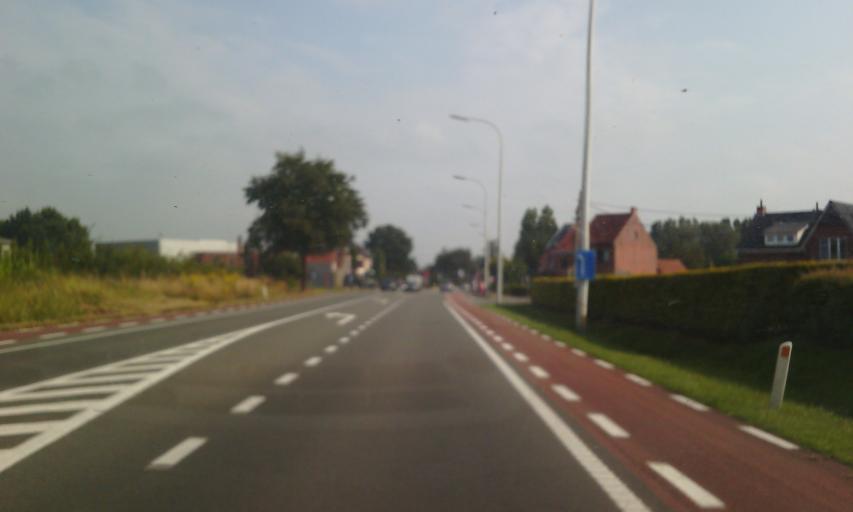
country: BE
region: Flanders
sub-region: Provincie Oost-Vlaanderen
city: Waarschoot
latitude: 51.1297
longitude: 3.6072
